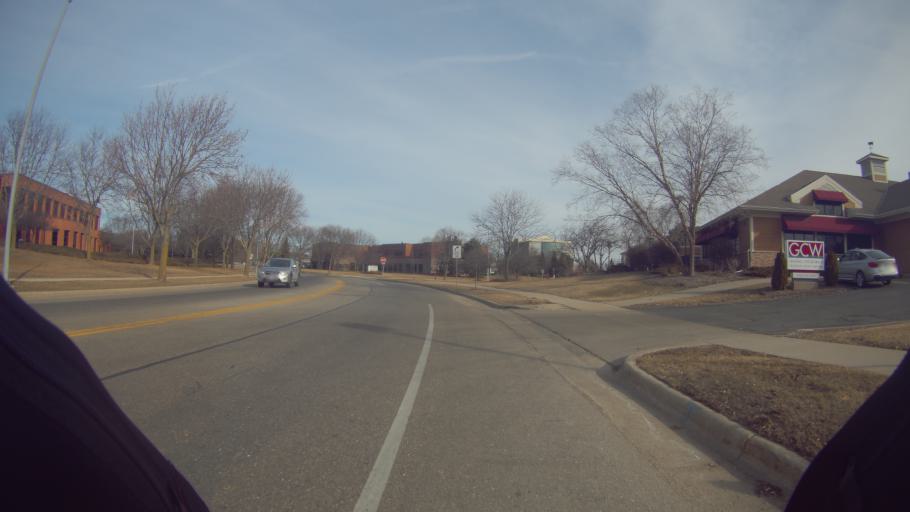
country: US
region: Wisconsin
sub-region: Dane County
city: Middleton
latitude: 43.0796
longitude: -89.5244
